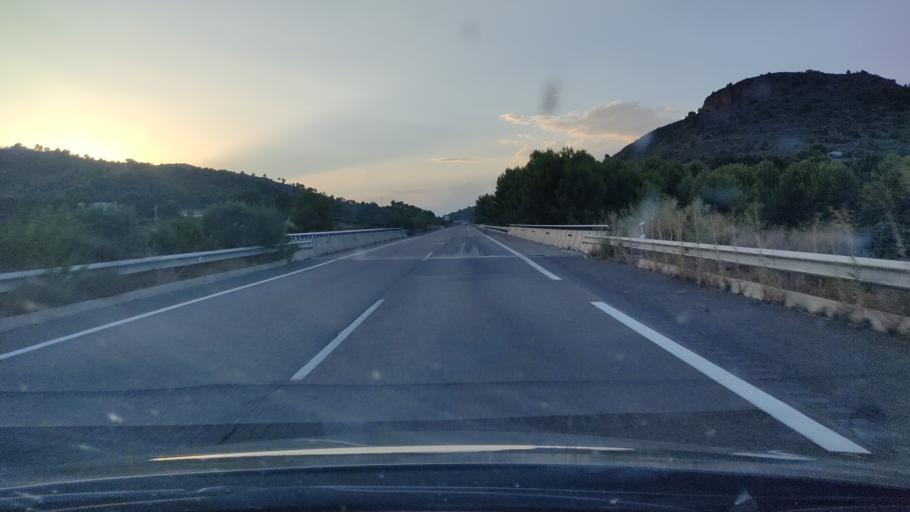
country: ES
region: Valencia
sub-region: Provincia de Valencia
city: Algimia de Alfara
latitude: 39.7477
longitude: -0.3725
